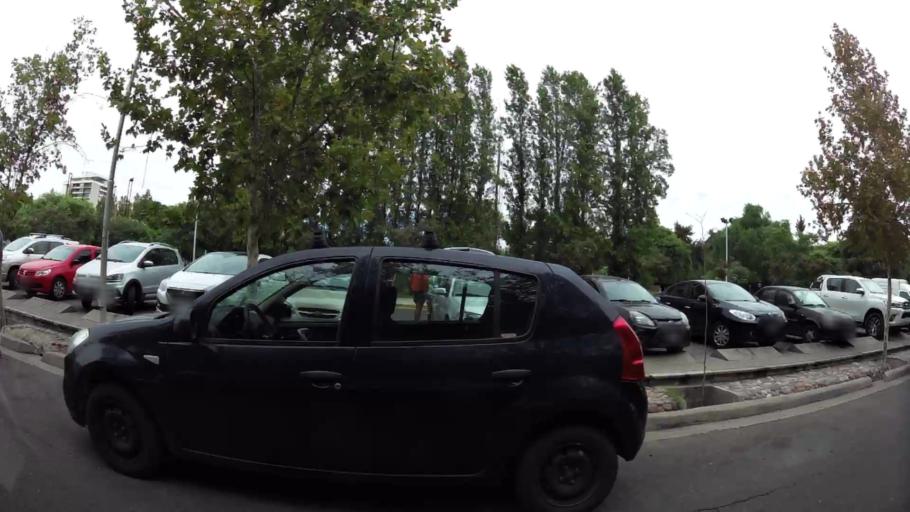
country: AR
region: Mendoza
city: Mendoza
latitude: -32.8738
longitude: -68.8418
